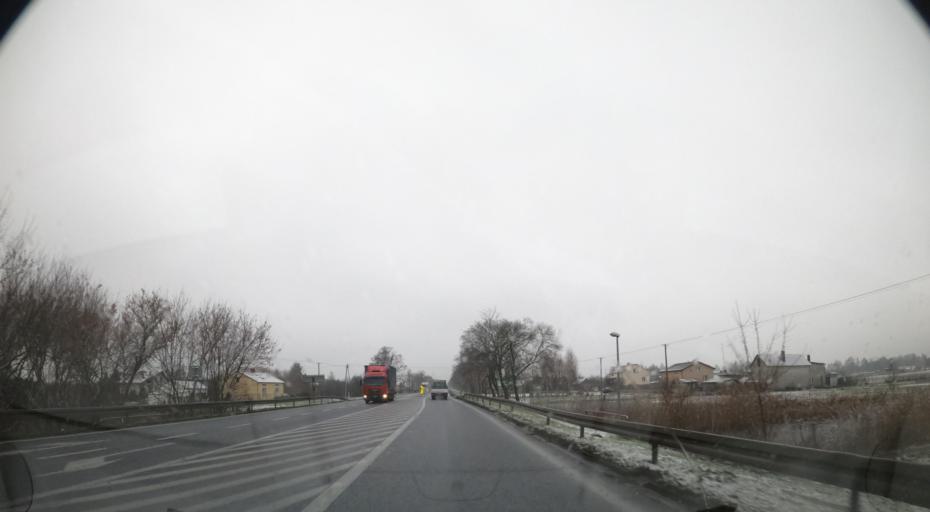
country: PL
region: Masovian Voivodeship
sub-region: Powiat sochaczewski
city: Paprotnia
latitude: 52.2133
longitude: 20.4153
